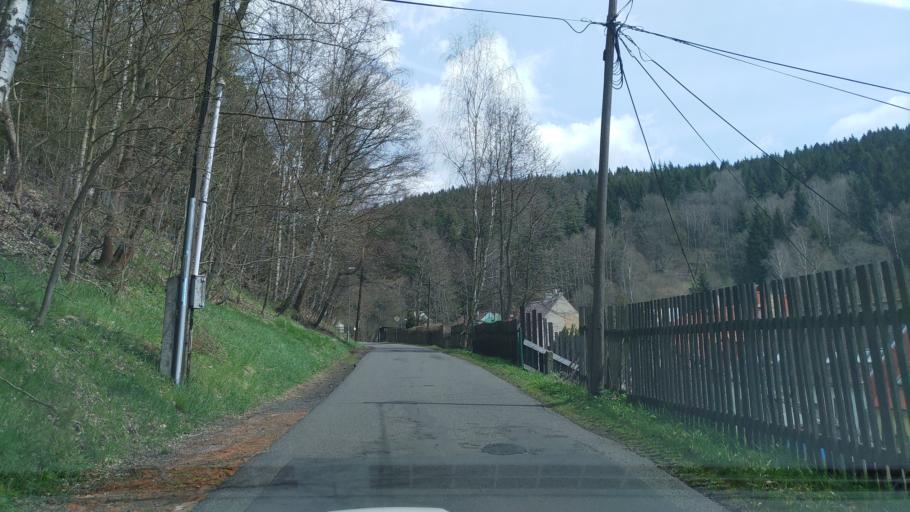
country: CZ
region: Karlovarsky
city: Jachymov
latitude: 50.3598
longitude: 12.9415
